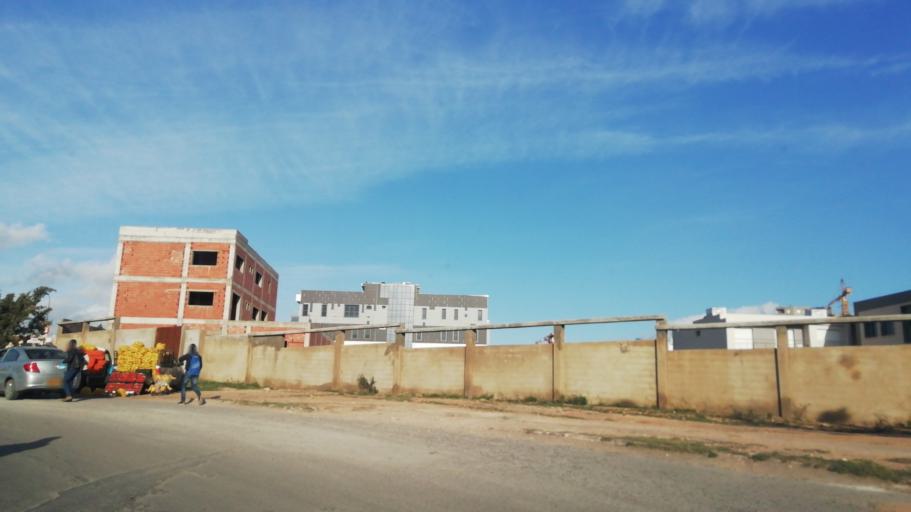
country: DZ
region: Oran
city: Bir el Djir
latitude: 35.7063
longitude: -0.5715
